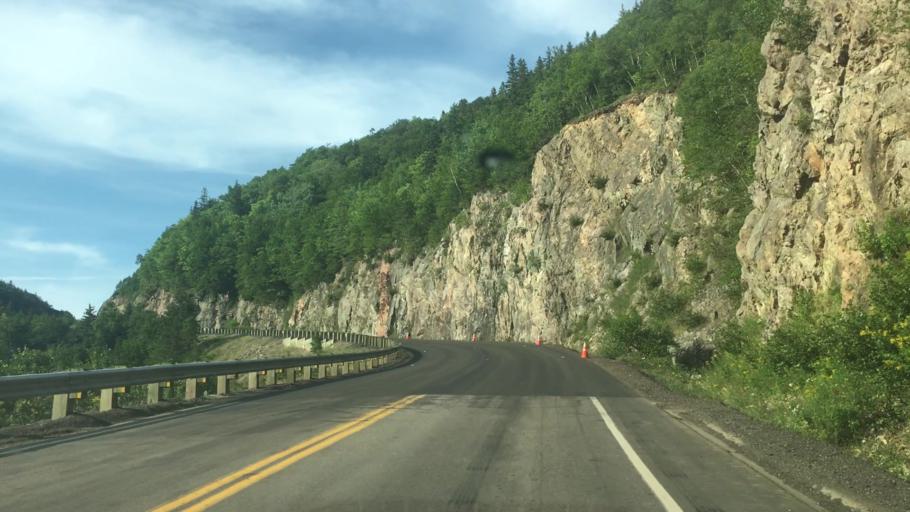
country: CA
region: Nova Scotia
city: Sydney Mines
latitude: 46.8168
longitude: -60.6512
